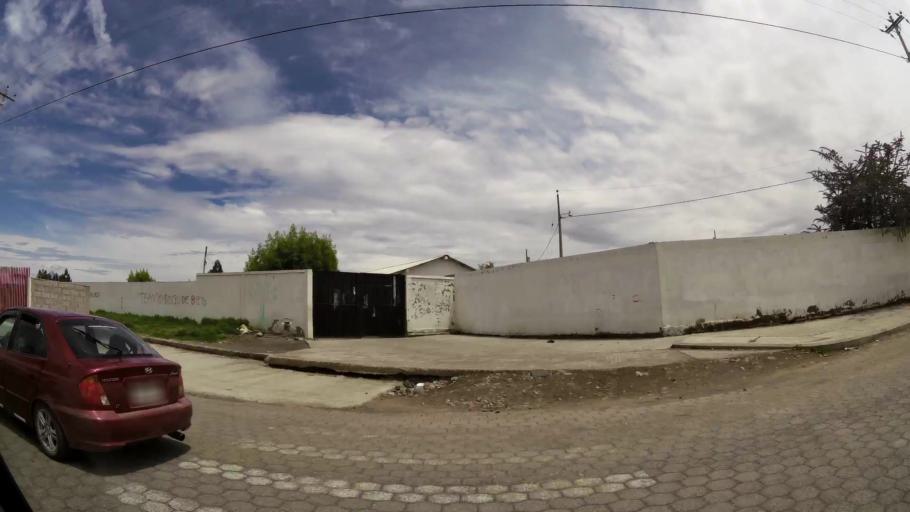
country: EC
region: Cotopaxi
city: San Miguel de Salcedo
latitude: -1.0408
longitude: -78.5841
